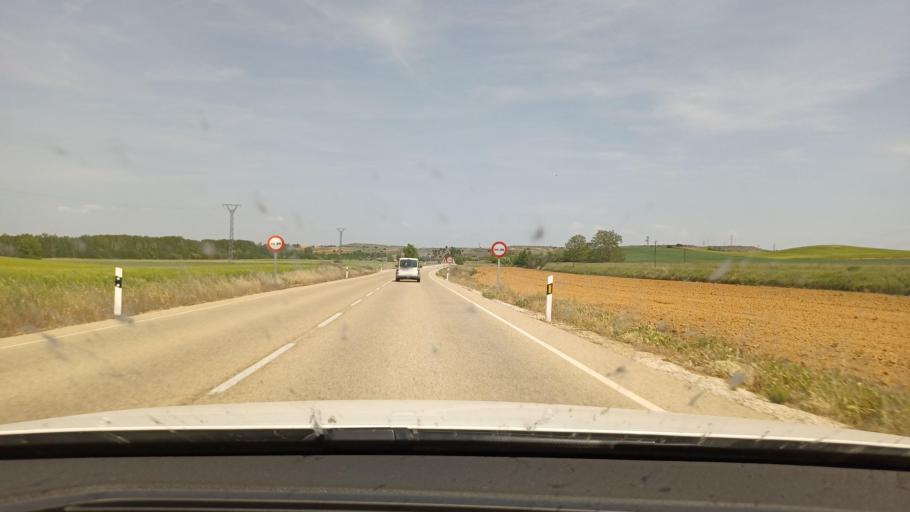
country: ES
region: Castille and Leon
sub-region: Provincia de Soria
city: Barca
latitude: 41.4653
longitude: -2.6252
